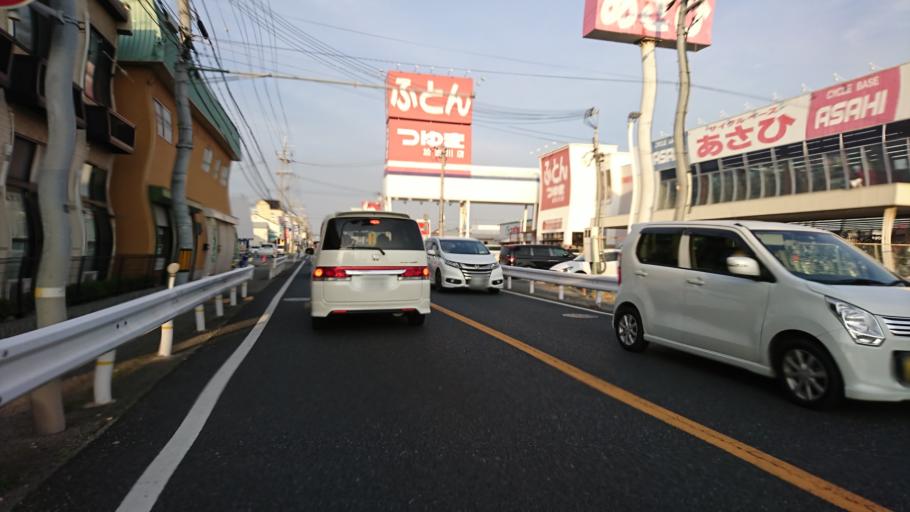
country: JP
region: Hyogo
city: Kakogawacho-honmachi
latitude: 34.7366
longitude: 134.8540
